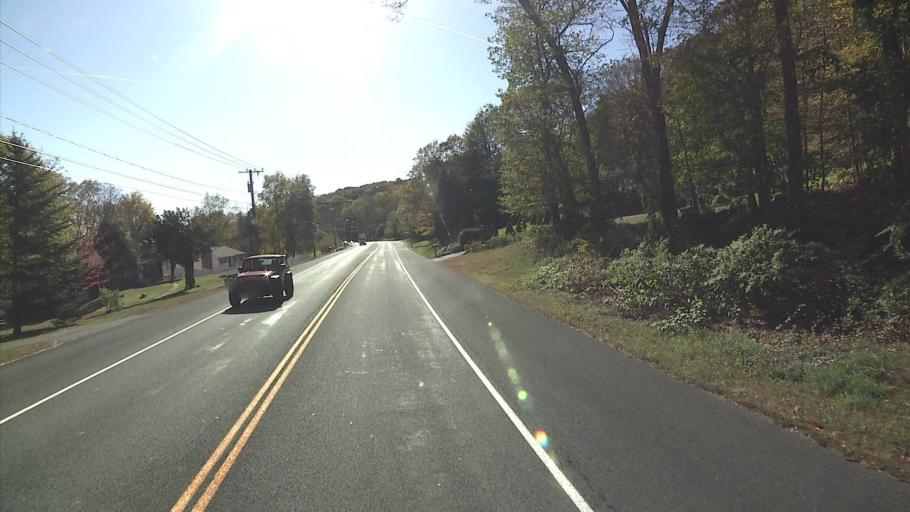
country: US
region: Connecticut
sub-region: Tolland County
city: Coventry Lake
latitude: 41.7755
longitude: -72.4153
